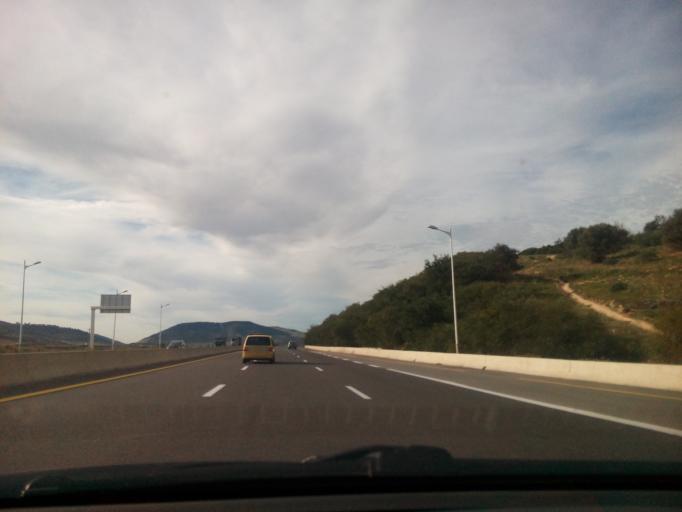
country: DZ
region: Sidi Bel Abbes
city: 'Ain el Berd
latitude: 35.4302
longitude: -0.4596
